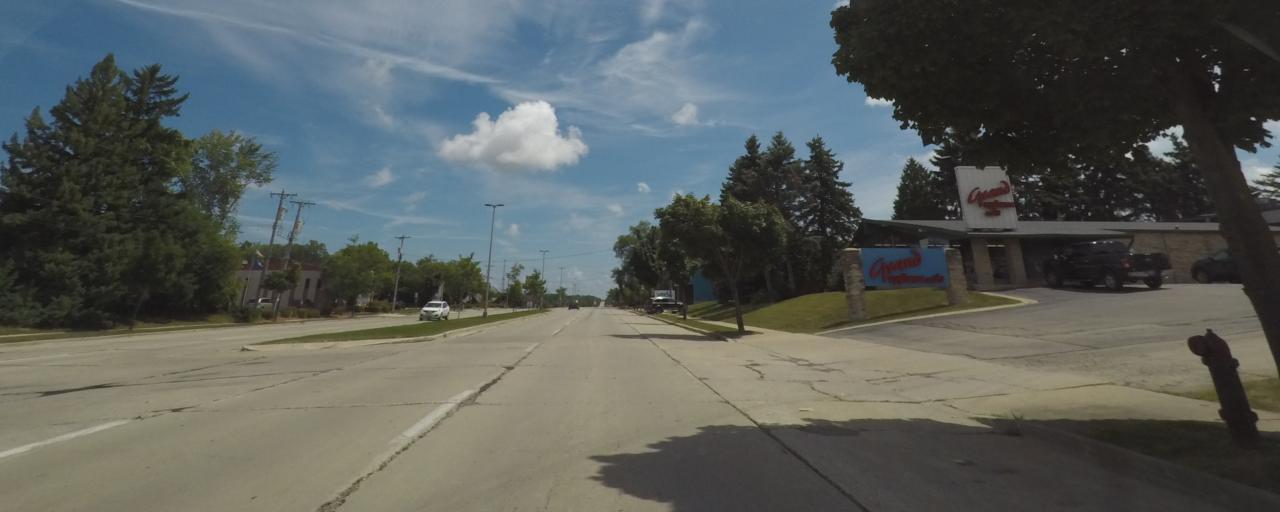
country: US
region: Wisconsin
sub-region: Milwaukee County
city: Greenfield
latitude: 42.9593
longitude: -87.9962
